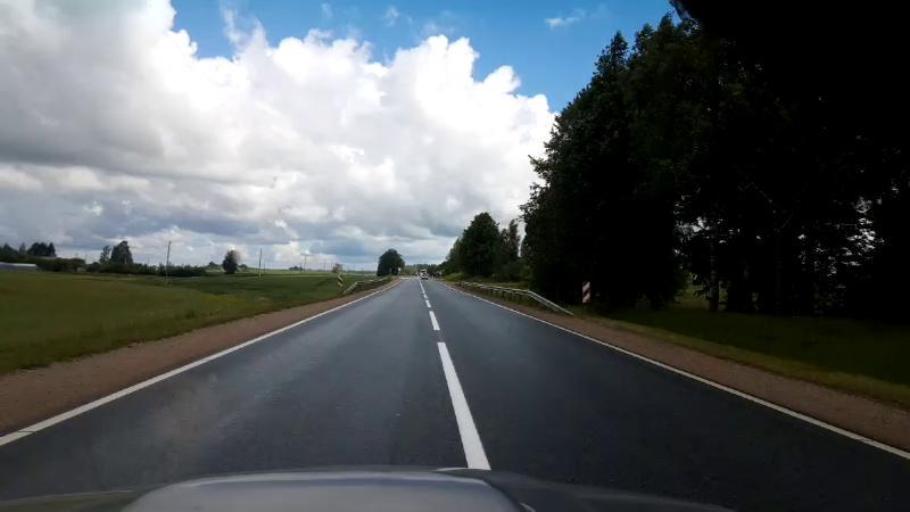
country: LV
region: Bauskas Rajons
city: Bauska
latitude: 56.5009
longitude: 24.1744
